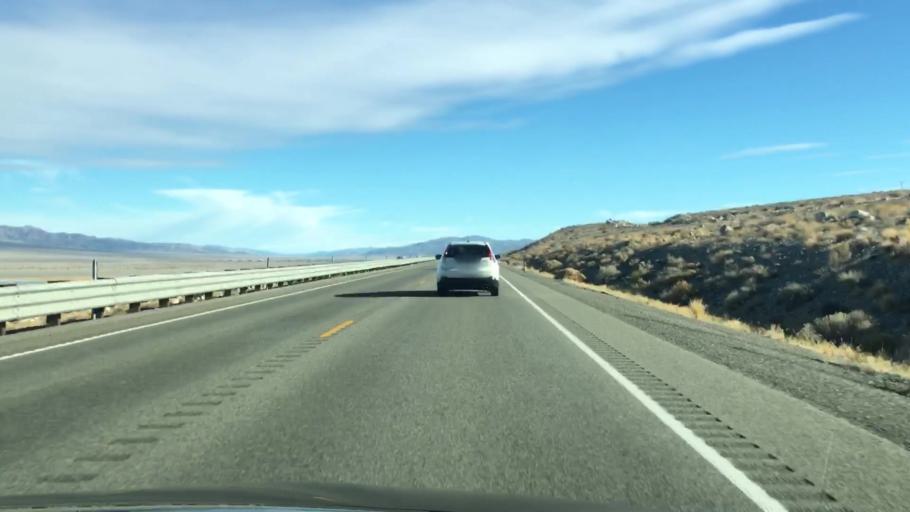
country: US
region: Nevada
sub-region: Mineral County
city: Hawthorne
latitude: 38.6149
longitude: -118.7265
